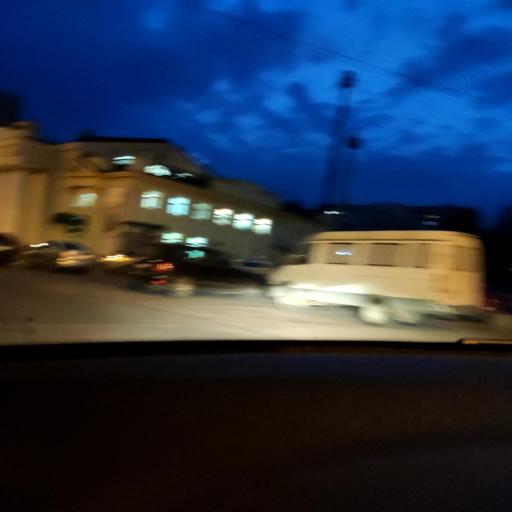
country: RU
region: Samara
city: Samara
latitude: 53.2006
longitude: 50.2191
